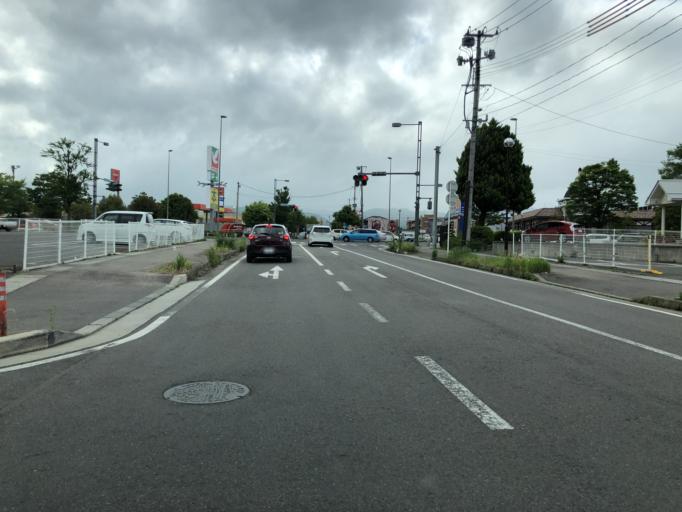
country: JP
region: Fukushima
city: Fukushima-shi
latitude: 37.7694
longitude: 140.4393
